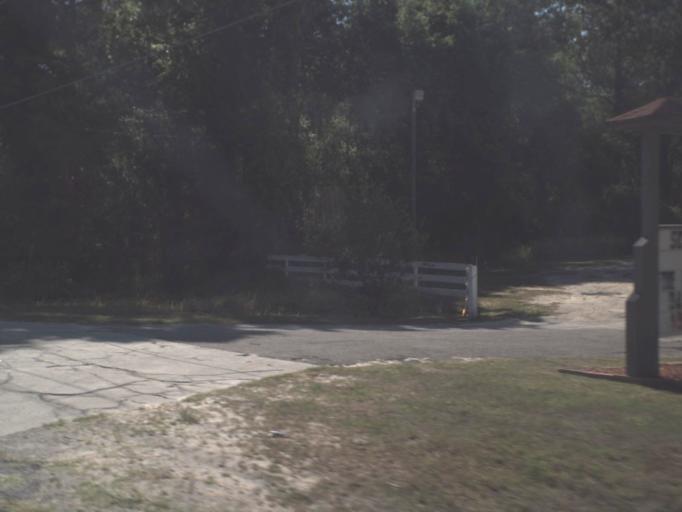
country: US
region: Florida
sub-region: Marion County
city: Dunnellon
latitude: 29.1440
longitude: -82.3776
